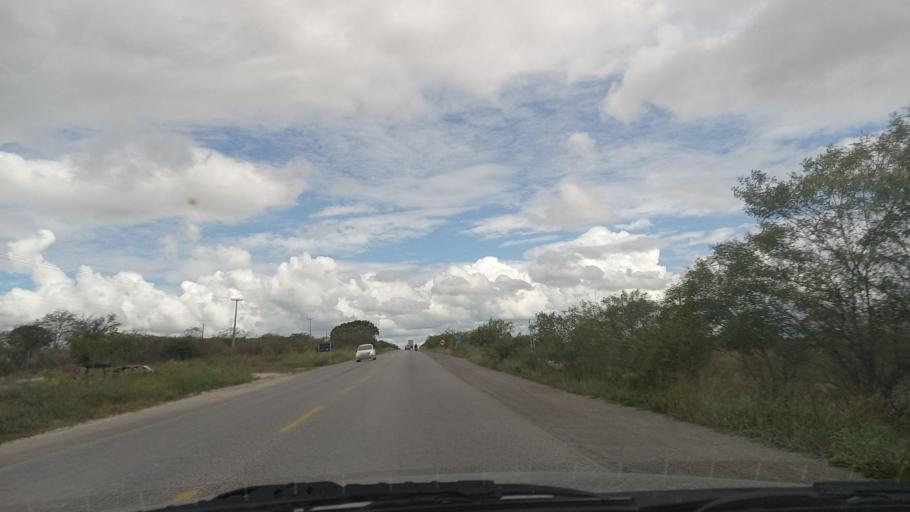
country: BR
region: Pernambuco
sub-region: Cachoeirinha
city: Cachoeirinha
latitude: -8.3683
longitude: -36.1725
